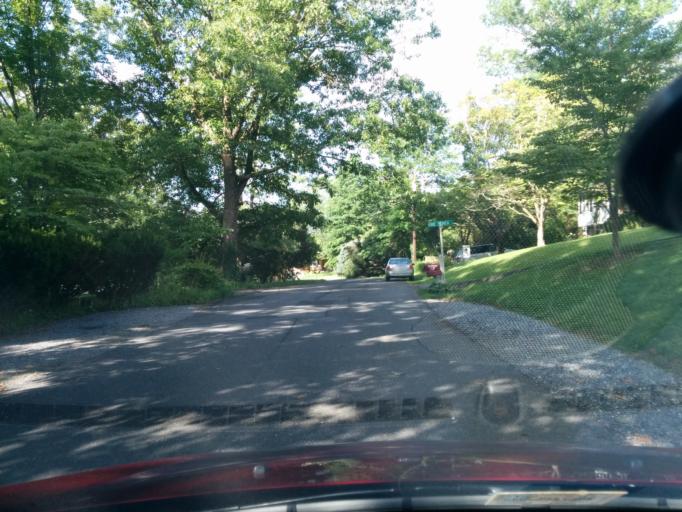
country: US
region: Virginia
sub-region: City of Lexington
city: Lexington
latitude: 37.7811
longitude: -79.4555
